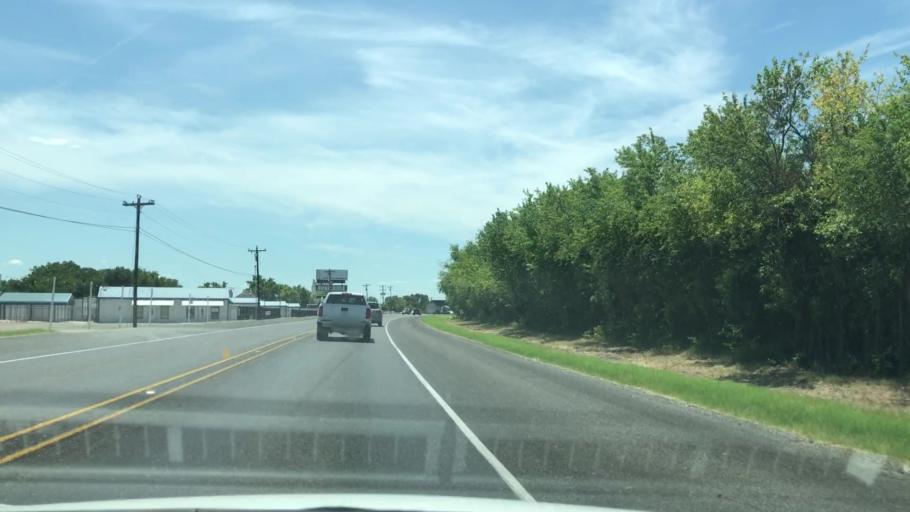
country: US
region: Texas
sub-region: Collin County
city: Lavon
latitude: 33.0148
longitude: -96.4570
